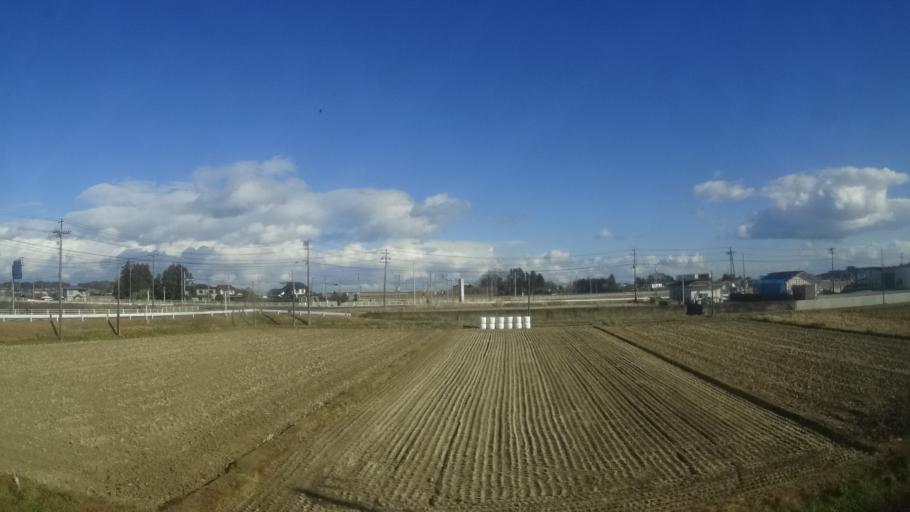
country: JP
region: Fukushima
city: Namie
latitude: 37.6936
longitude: 140.9733
